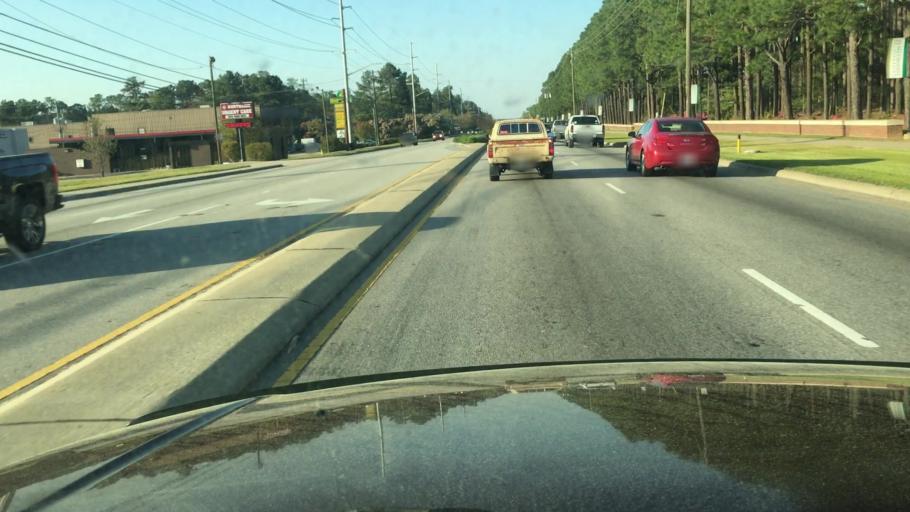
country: US
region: North Carolina
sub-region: Cumberland County
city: Fayetteville
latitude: 35.1325
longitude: -78.8773
